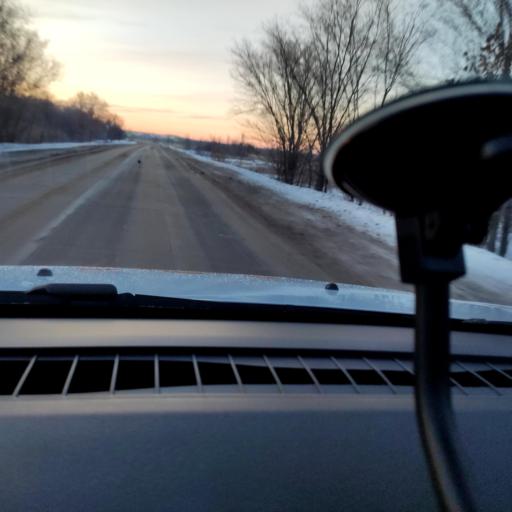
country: RU
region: Samara
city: Dubovyy Umet
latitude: 53.0946
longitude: 50.2303
